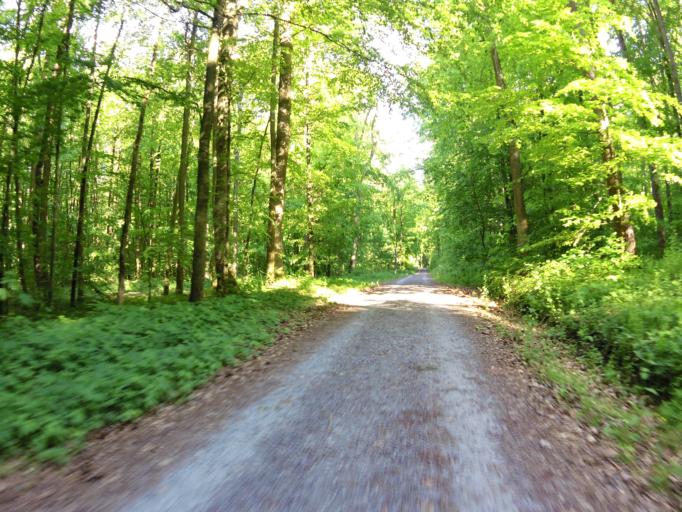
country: DE
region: Bavaria
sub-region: Regierungsbezirk Unterfranken
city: Reichenberg
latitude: 49.7507
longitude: 9.9104
